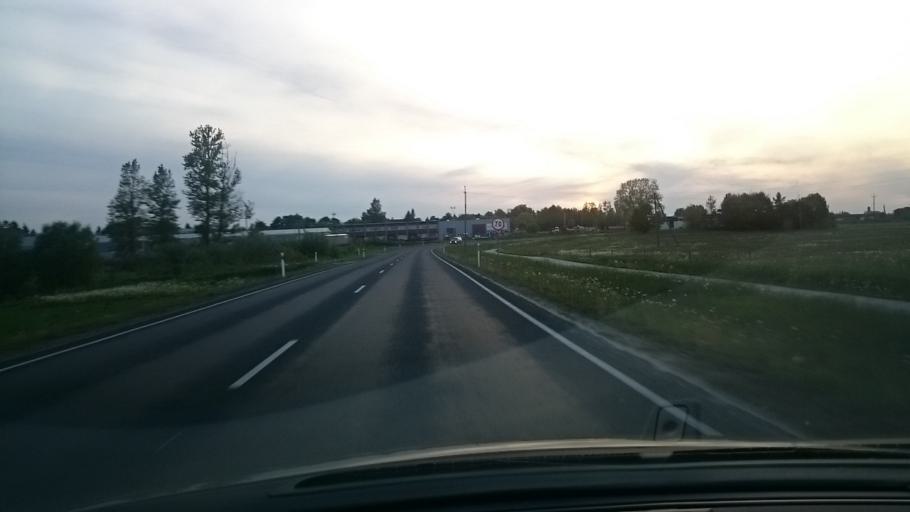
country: EE
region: Jaervamaa
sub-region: Tueri vald
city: Sarevere
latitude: 58.7800
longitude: 25.4387
